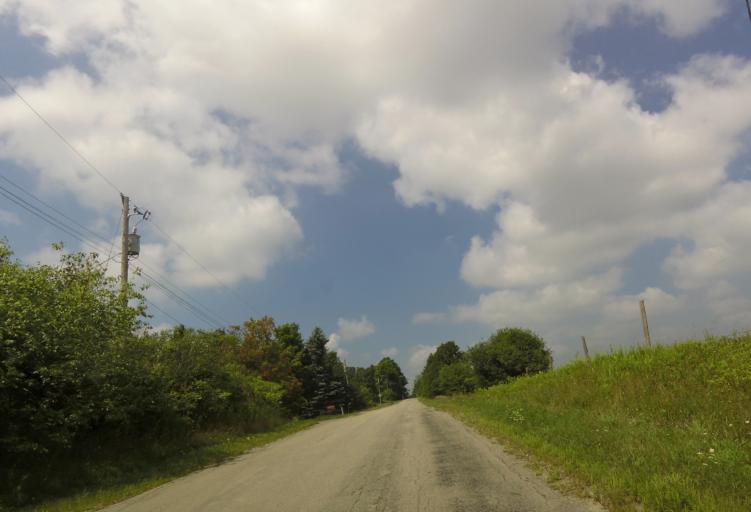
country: CA
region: Ontario
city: Oshawa
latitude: 44.0004
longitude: -78.8762
